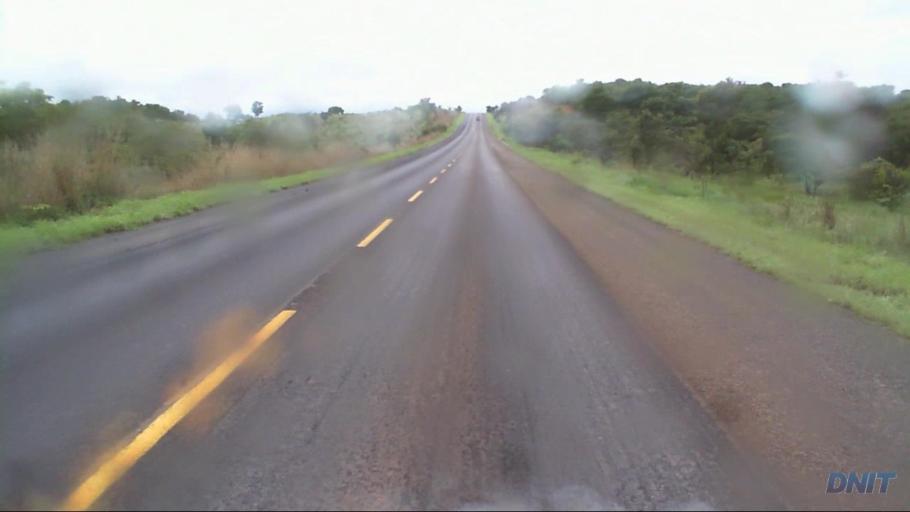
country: BR
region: Goias
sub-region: Padre Bernardo
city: Padre Bernardo
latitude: -15.1974
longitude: -48.4460
